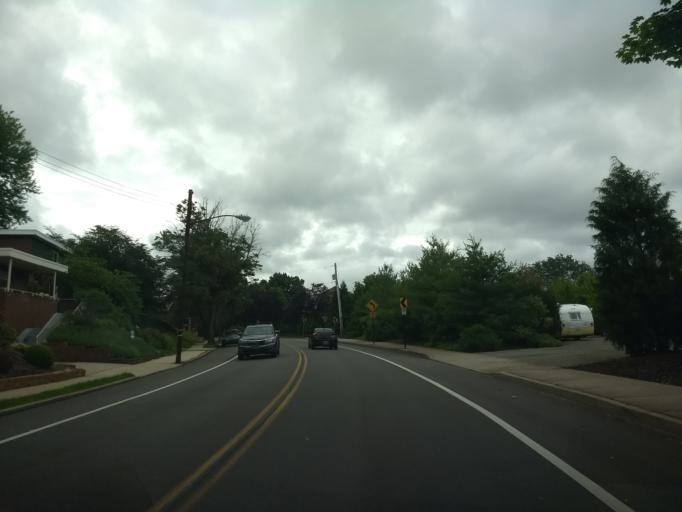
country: US
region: Pennsylvania
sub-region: Allegheny County
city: Homestead
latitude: 40.4215
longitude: -79.9182
